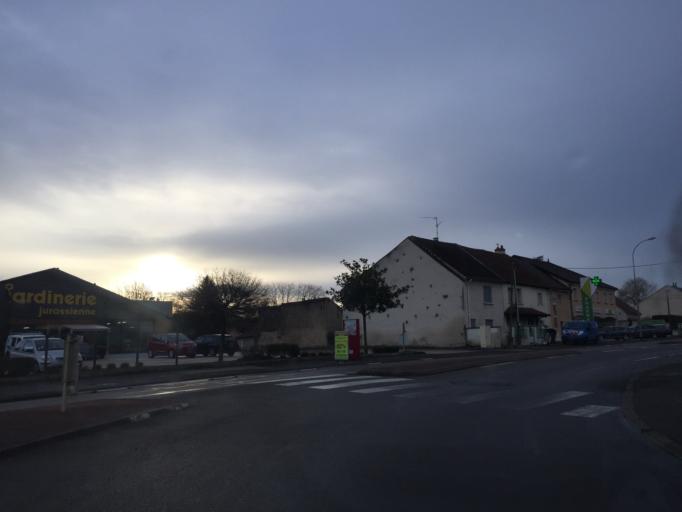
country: FR
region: Franche-Comte
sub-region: Departement du Jura
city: Dole
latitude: 47.0727
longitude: 5.4975
